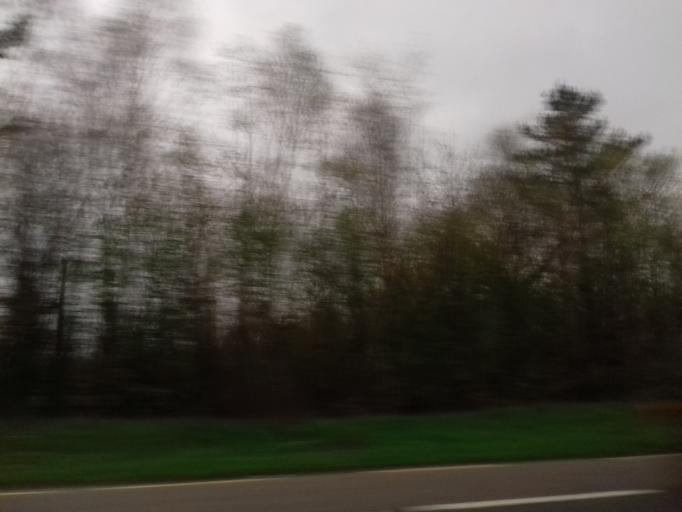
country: IE
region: Munster
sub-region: County Limerick
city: Rathkeale
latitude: 52.5307
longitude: -8.9135
